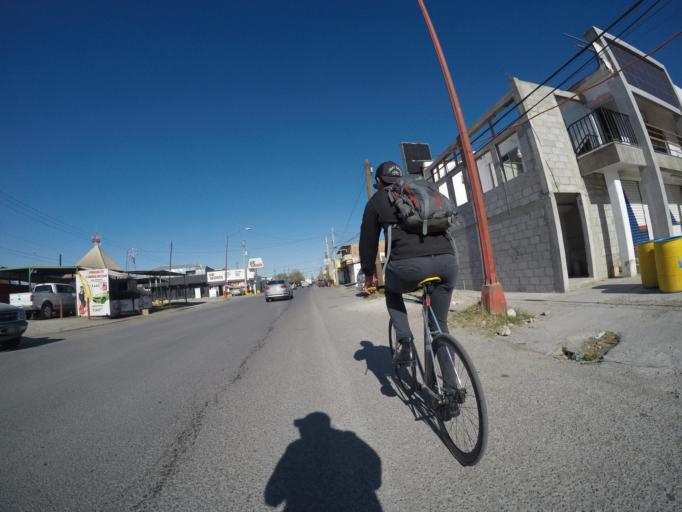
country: MX
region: Chihuahua
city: Ciudad Juarez
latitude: 31.7323
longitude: -106.4533
